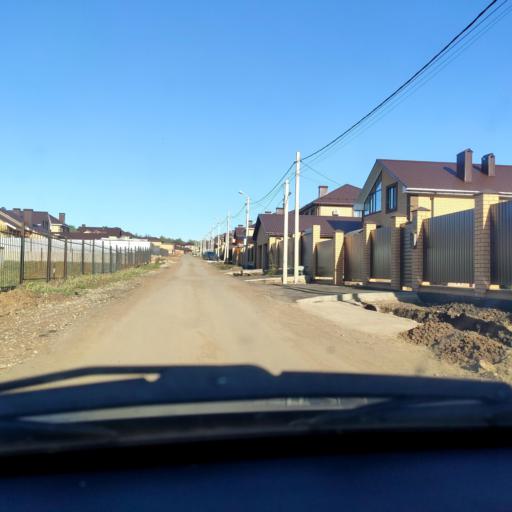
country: RU
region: Bashkortostan
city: Mikhaylovka
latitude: 54.8326
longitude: 55.8710
